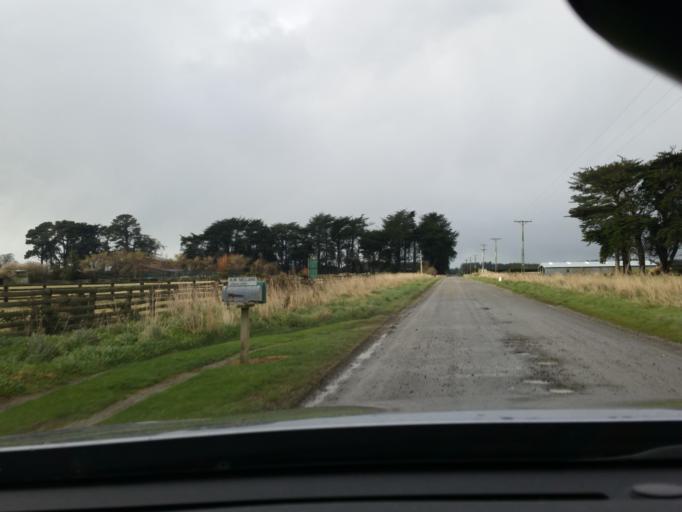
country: NZ
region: Southland
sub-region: Invercargill City
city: Invercargill
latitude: -46.3558
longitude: 168.4366
